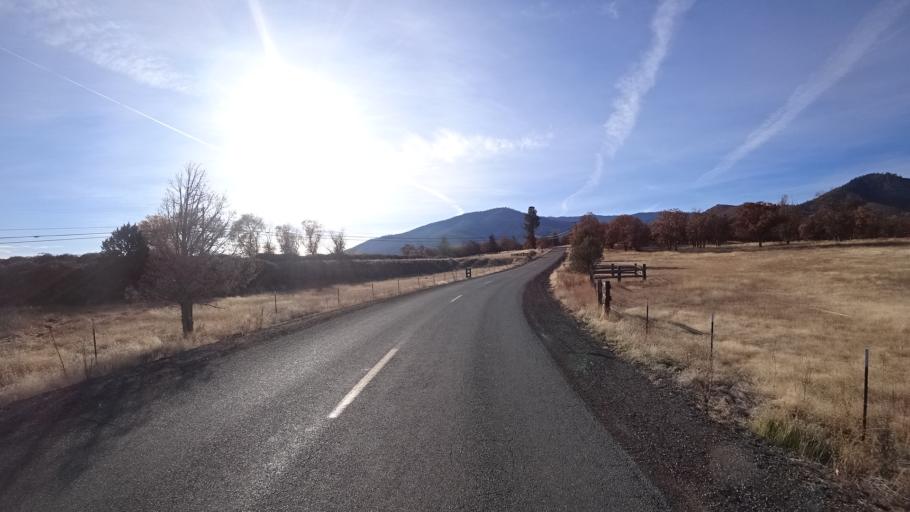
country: US
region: California
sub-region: Siskiyou County
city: Yreka
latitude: 41.6725
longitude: -122.6232
